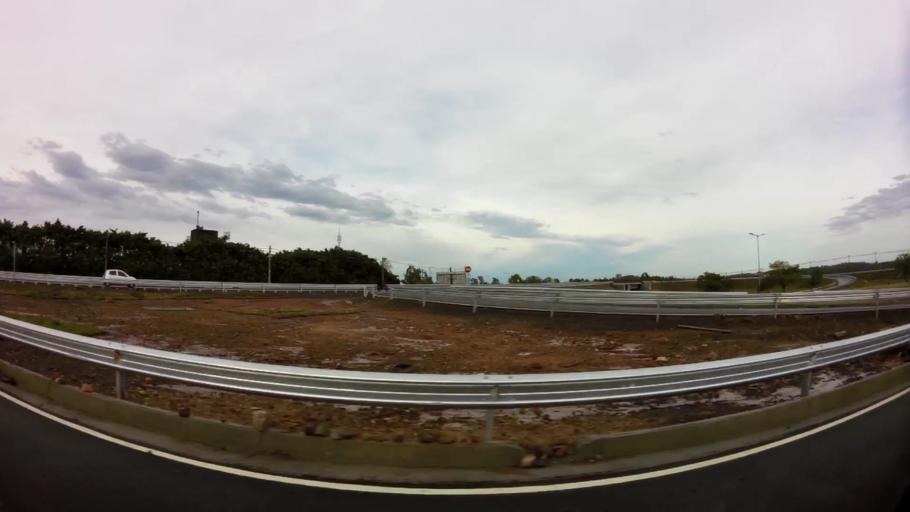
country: PY
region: Central
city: Fernando de la Mora
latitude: -25.2618
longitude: -57.5173
